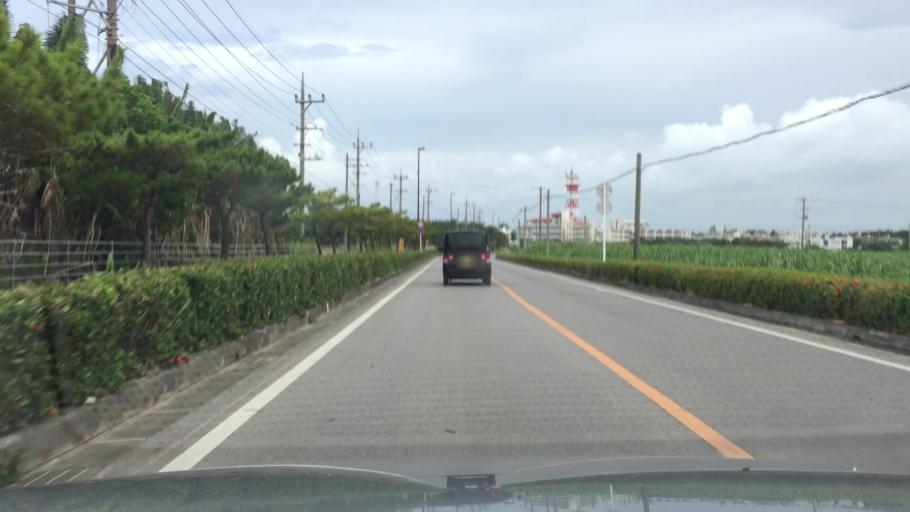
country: JP
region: Okinawa
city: Ishigaki
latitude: 24.3558
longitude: 124.1574
